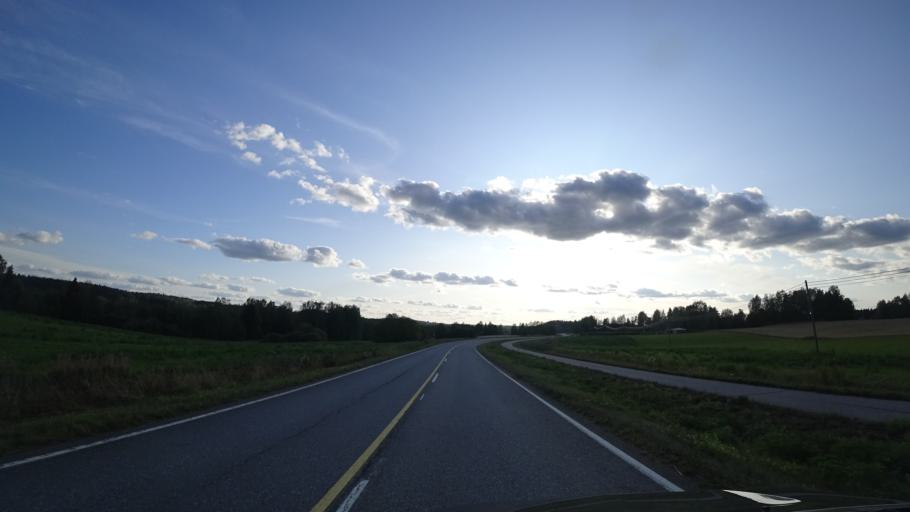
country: FI
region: Haeme
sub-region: Haemeenlinna
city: Lammi
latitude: 61.0815
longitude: 25.0517
